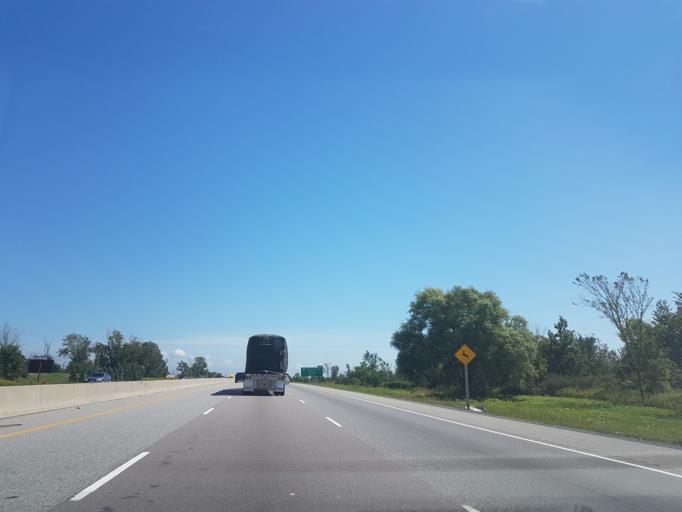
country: CA
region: Ontario
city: Kingston
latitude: 44.2807
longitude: -76.5575
